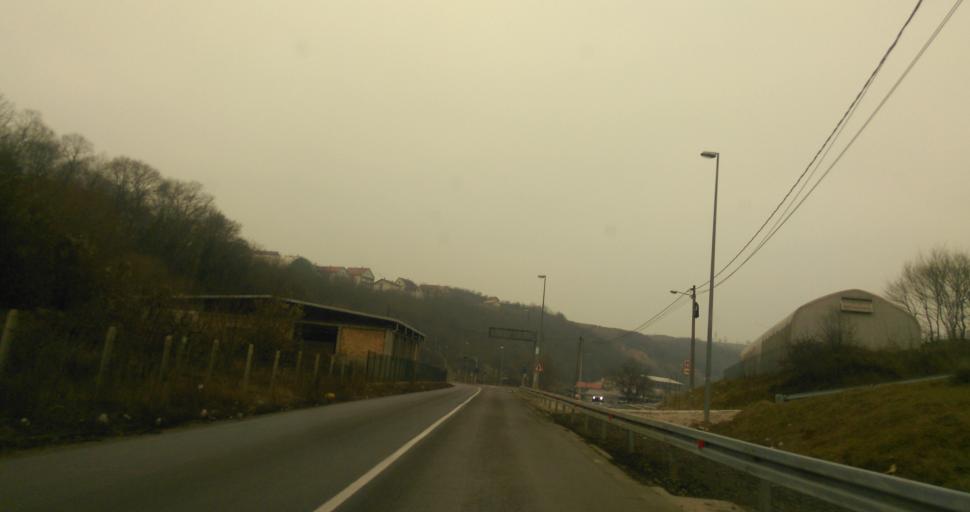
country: RS
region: Central Serbia
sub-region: Belgrade
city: Rakovica
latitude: 44.7234
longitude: 20.4529
